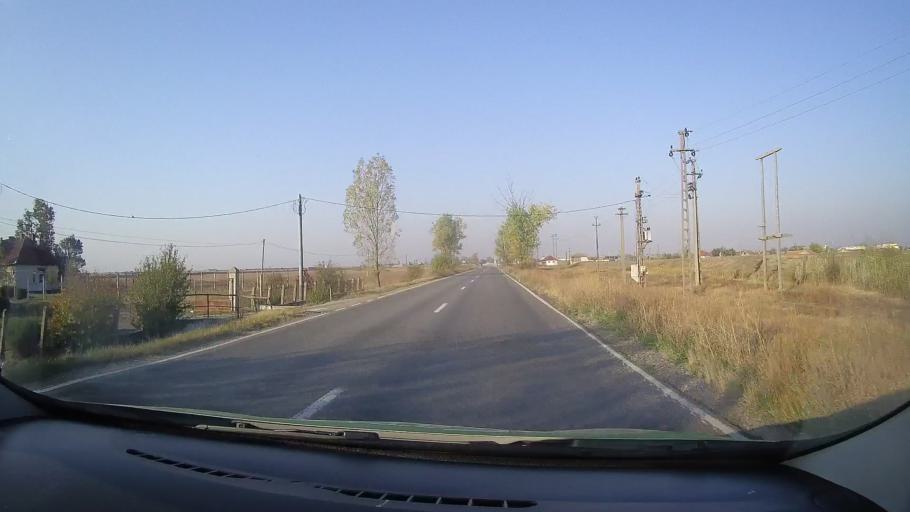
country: RO
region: Arad
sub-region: Comuna Socodor
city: Socodor
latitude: 46.5048
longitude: 21.4551
